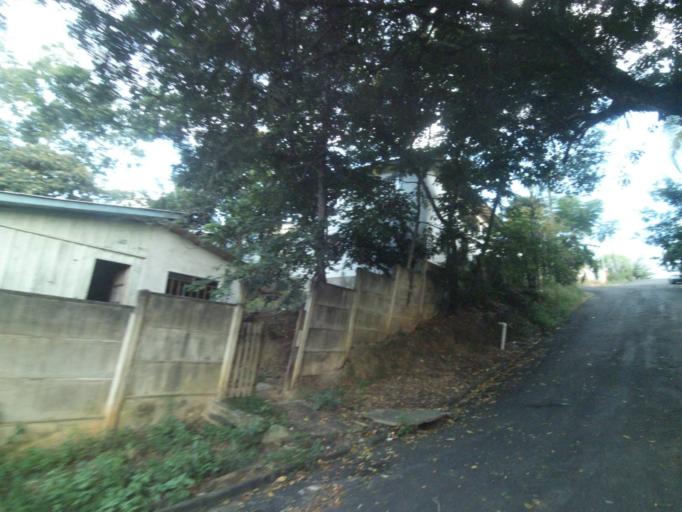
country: BR
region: Parana
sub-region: Telemaco Borba
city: Telemaco Borba
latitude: -24.3221
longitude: -50.6415
